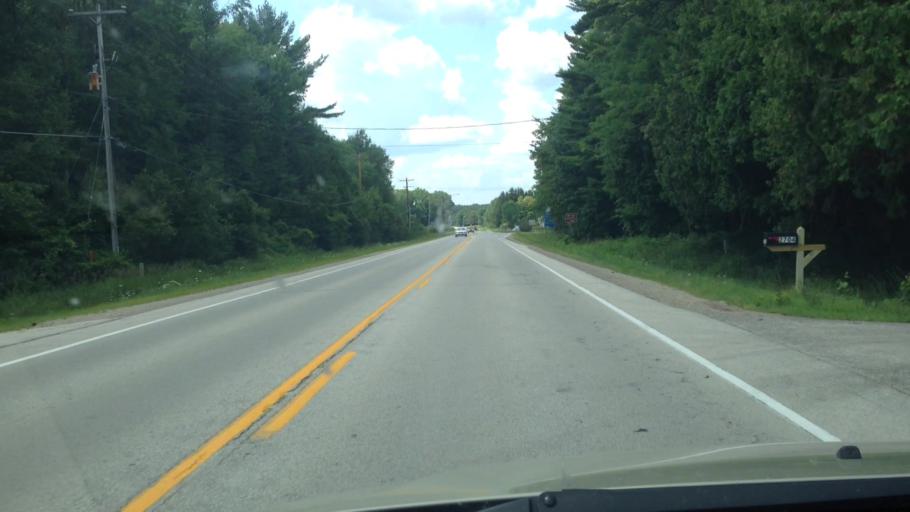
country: US
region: Wisconsin
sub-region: Brown County
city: Suamico
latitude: 44.6435
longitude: -88.0875
